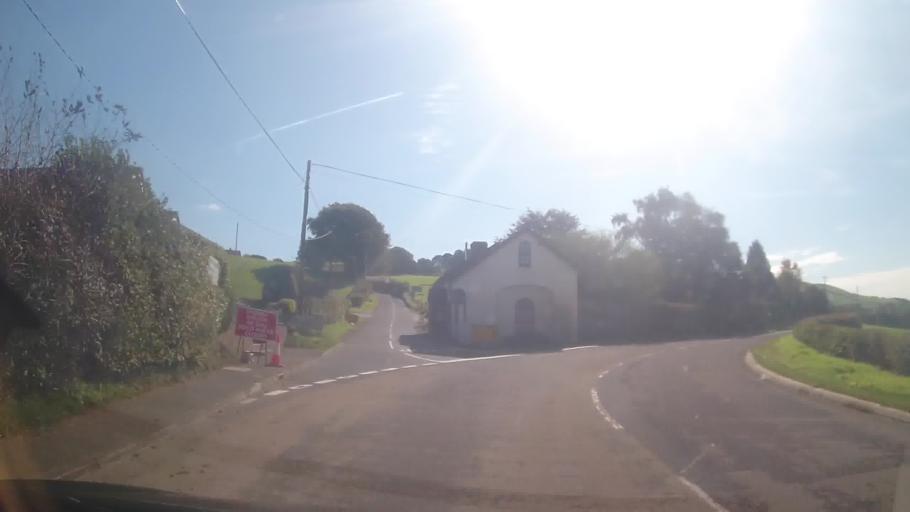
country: GB
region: Wales
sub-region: Sir Powys
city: Newtown
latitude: 52.4742
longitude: -3.3174
